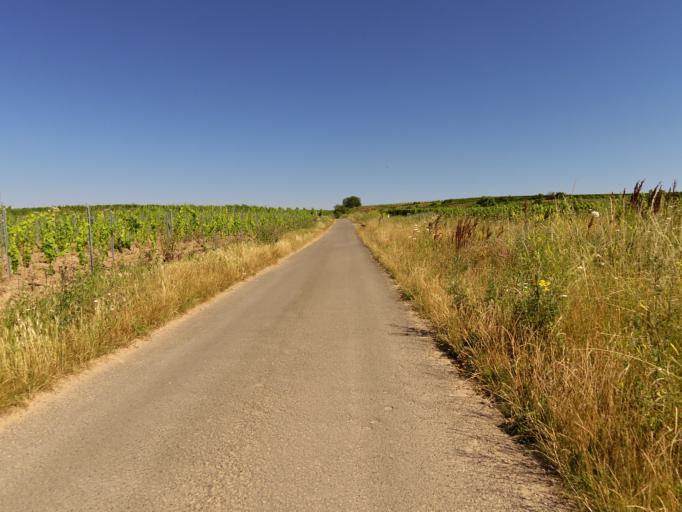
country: DE
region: Rheinland-Pfalz
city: Dackenheim
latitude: 49.5187
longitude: 8.2021
